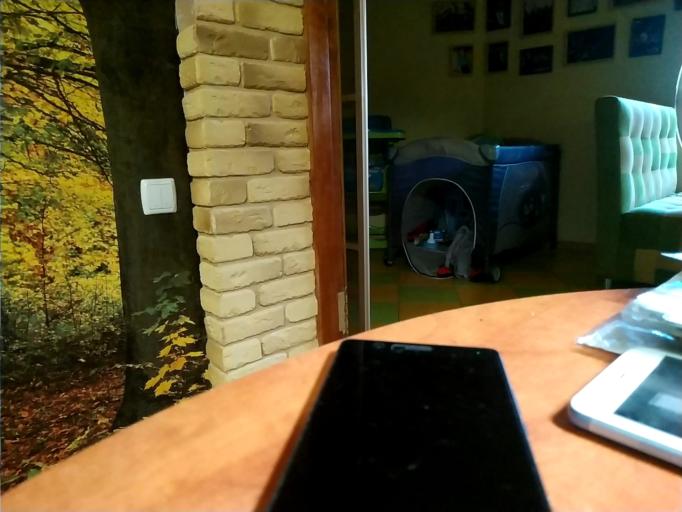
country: RU
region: Orjol
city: Znamenskoye
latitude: 53.5222
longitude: 35.4989
